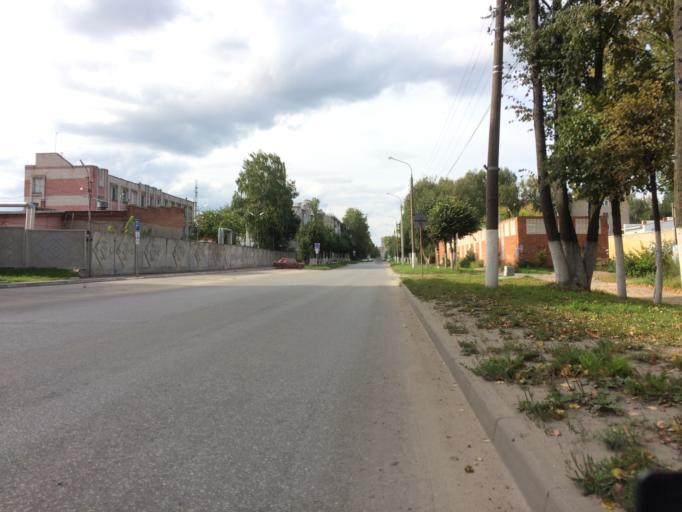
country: RU
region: Mariy-El
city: Yoshkar-Ola
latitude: 56.6332
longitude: 47.8741
